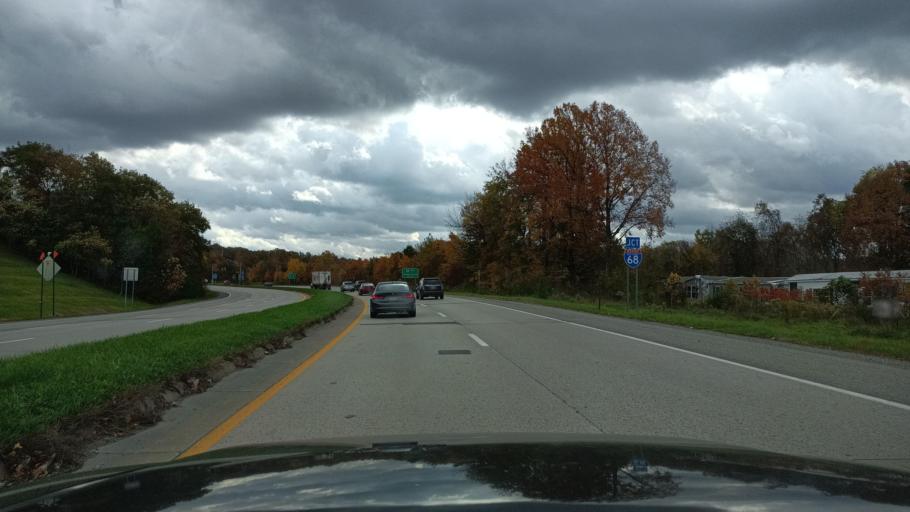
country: US
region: West Virginia
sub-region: Monongalia County
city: Brookhaven
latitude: 39.6477
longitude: -79.9000
